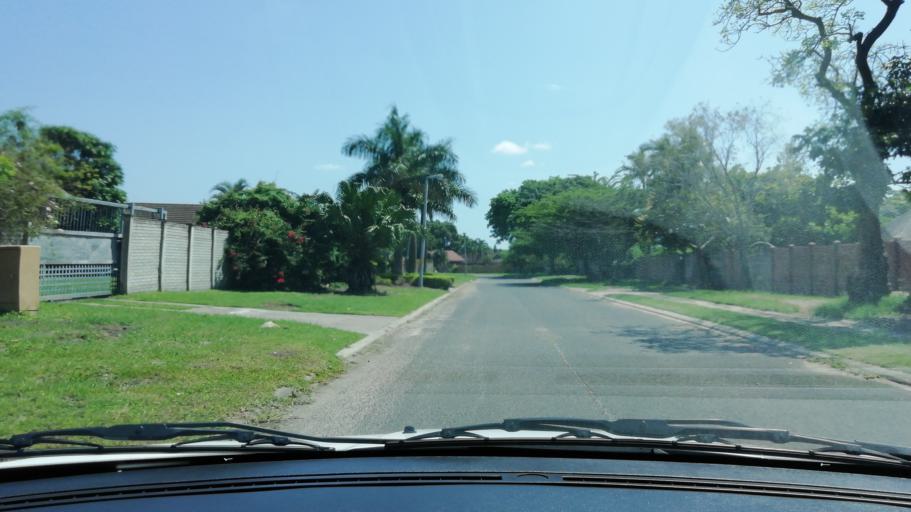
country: ZA
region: KwaZulu-Natal
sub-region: uThungulu District Municipality
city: Richards Bay
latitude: -28.7397
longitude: 32.0594
